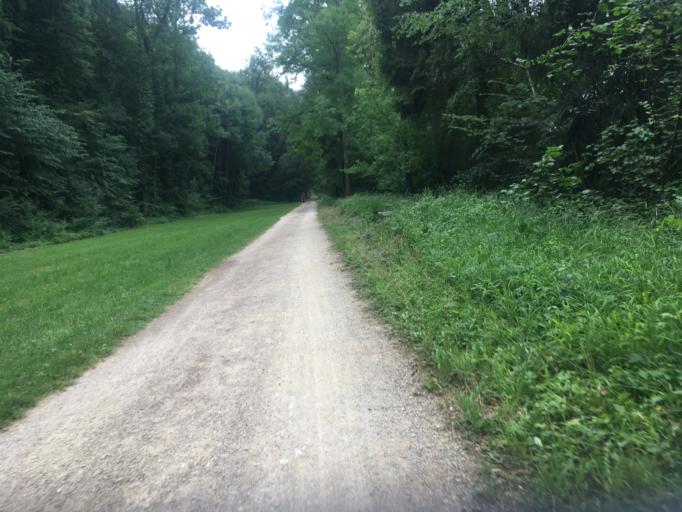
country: CH
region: Bern
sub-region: Jura bernois
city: La Neuveville
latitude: 47.0727
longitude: 7.1409
